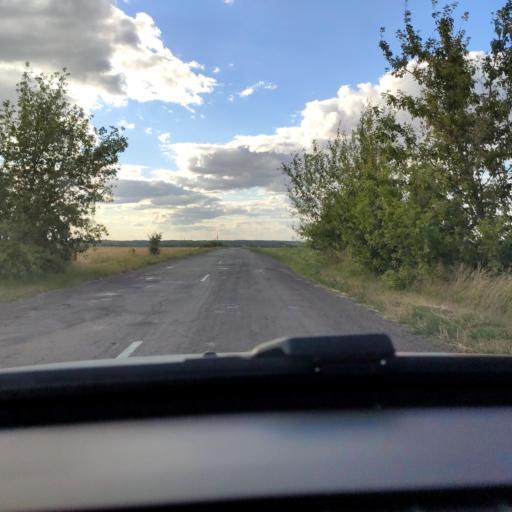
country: RU
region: Voronezj
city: Orlovo
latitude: 51.6351
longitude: 39.7658
